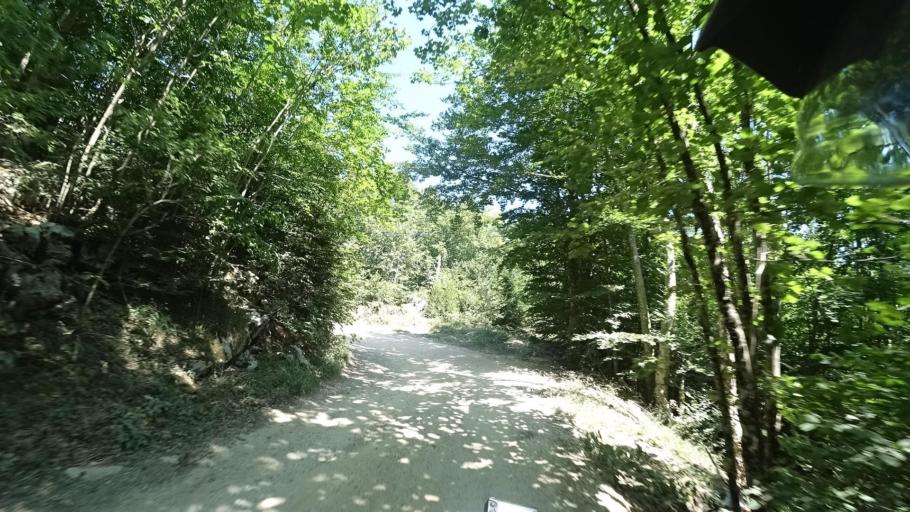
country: HR
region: Licko-Senjska
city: Popovaca
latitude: 44.5572
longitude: 15.2148
